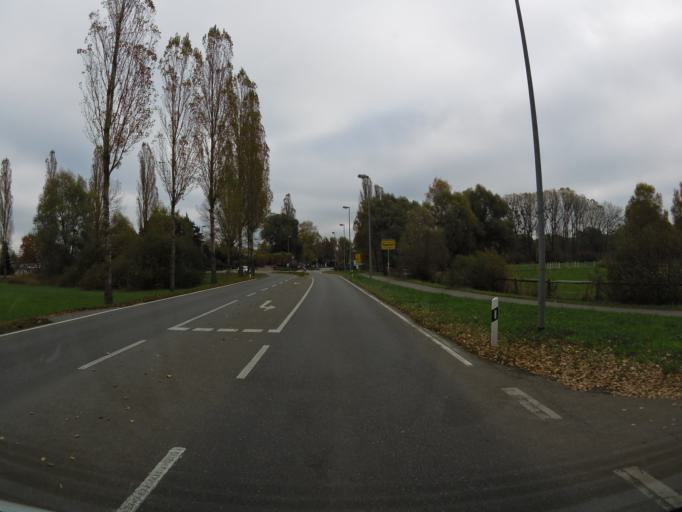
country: DE
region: Baden-Wuerttemberg
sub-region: Freiburg Region
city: Moos
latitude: 47.7378
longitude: 8.9472
